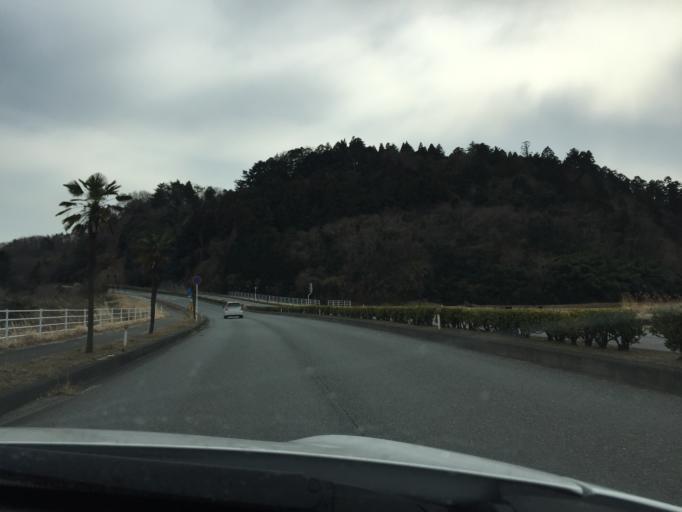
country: JP
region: Fukushima
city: Iwaki
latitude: 36.9909
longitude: 140.8252
